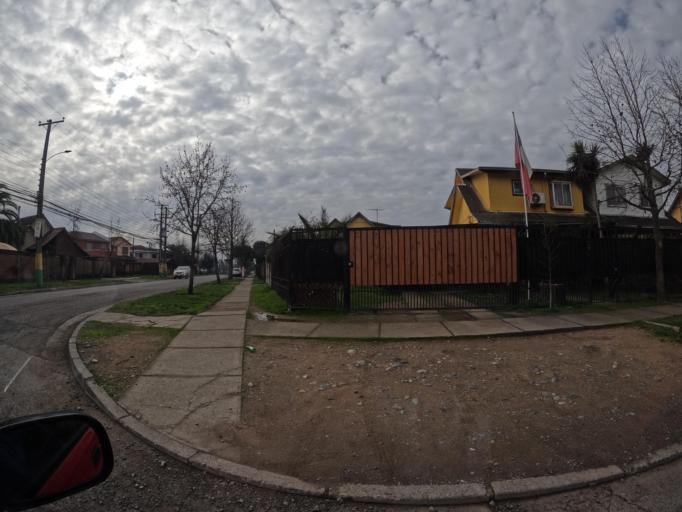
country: CL
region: Maule
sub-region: Provincia de Linares
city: Linares
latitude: -35.8334
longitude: -71.6009
